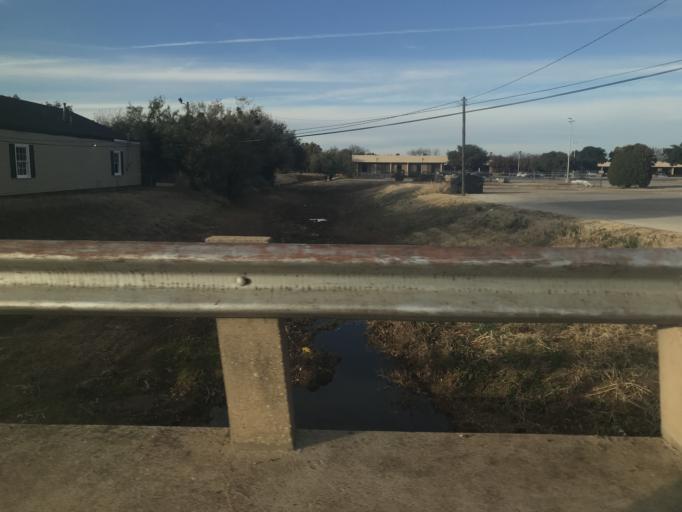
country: US
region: Texas
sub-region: Taylor County
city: Abilene
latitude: 32.4323
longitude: -99.7660
